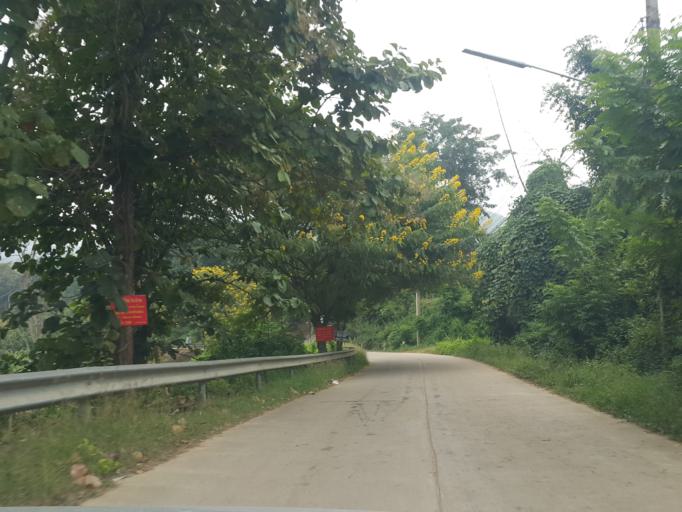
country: TH
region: Chiang Mai
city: Pai
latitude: 19.3578
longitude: 98.4472
